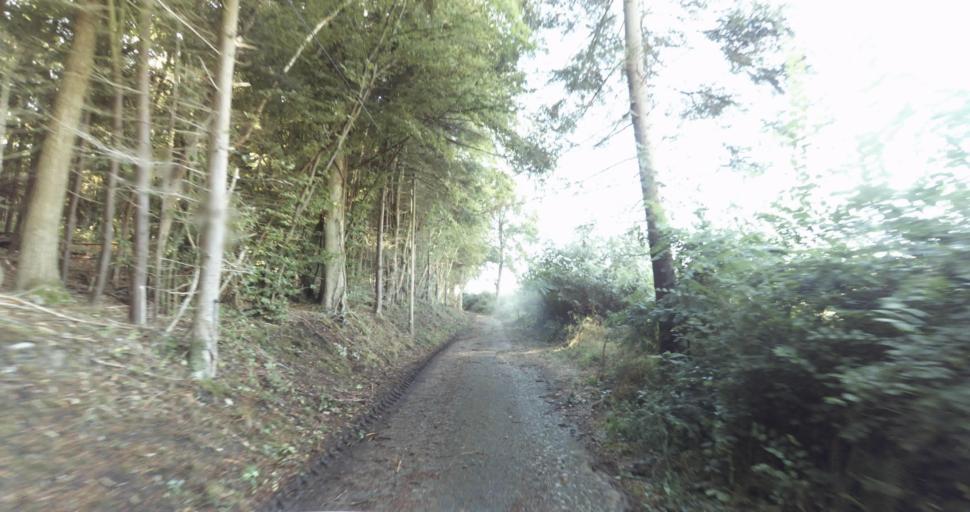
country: FR
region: Lower Normandy
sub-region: Departement de l'Orne
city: Vimoutiers
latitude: 48.9308
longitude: 0.2945
